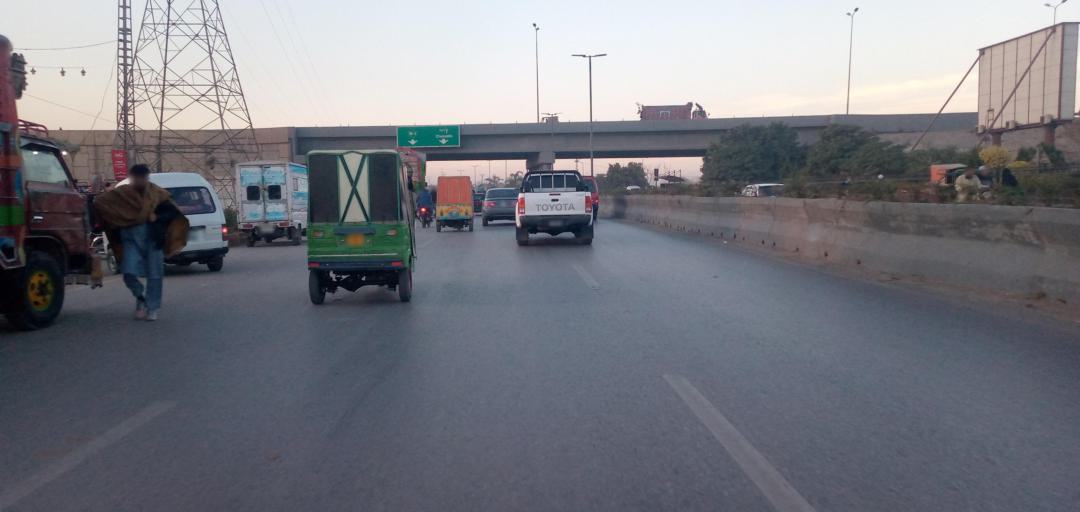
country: PK
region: Khyber Pakhtunkhwa
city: Peshawar
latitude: 34.0228
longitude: 71.6210
